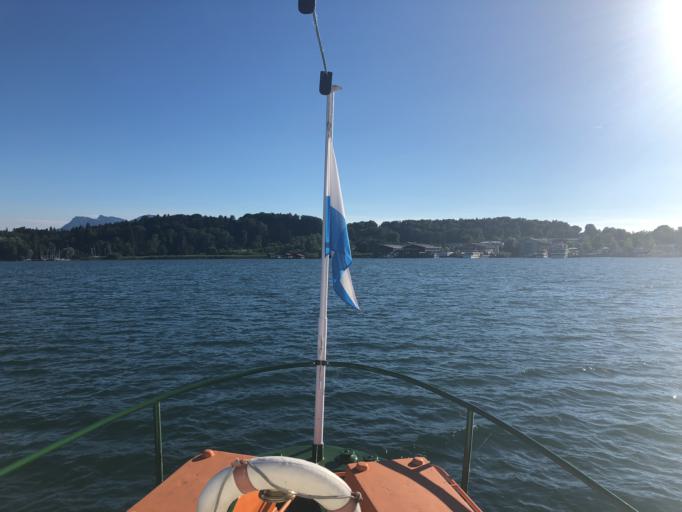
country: DE
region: Bavaria
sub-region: Upper Bavaria
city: Prien am Chiemsee
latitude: 47.8618
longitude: 12.3719
